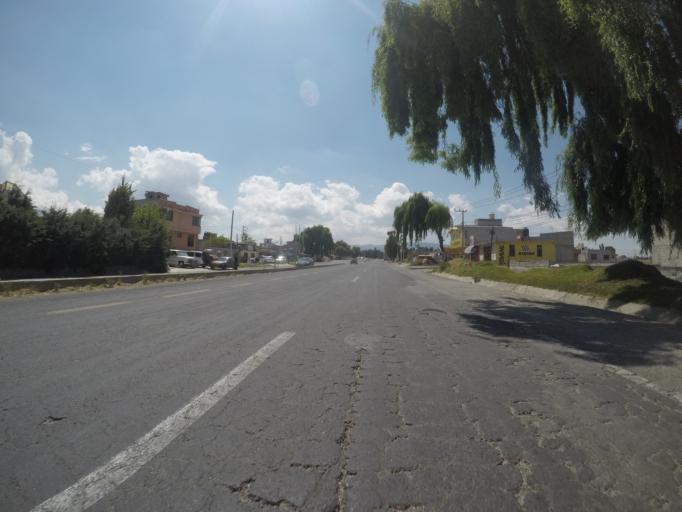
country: MX
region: Mexico
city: San Juan de las Huertas
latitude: 19.2506
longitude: -99.7587
